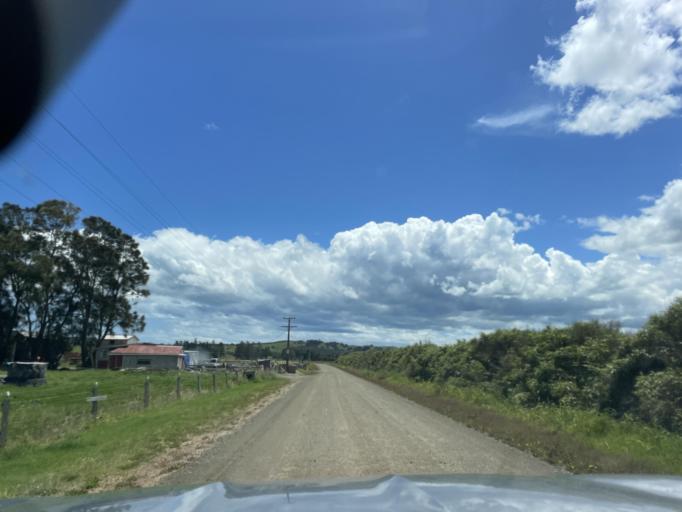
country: NZ
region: Northland
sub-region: Kaipara District
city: Dargaville
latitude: -35.8939
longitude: 173.9082
